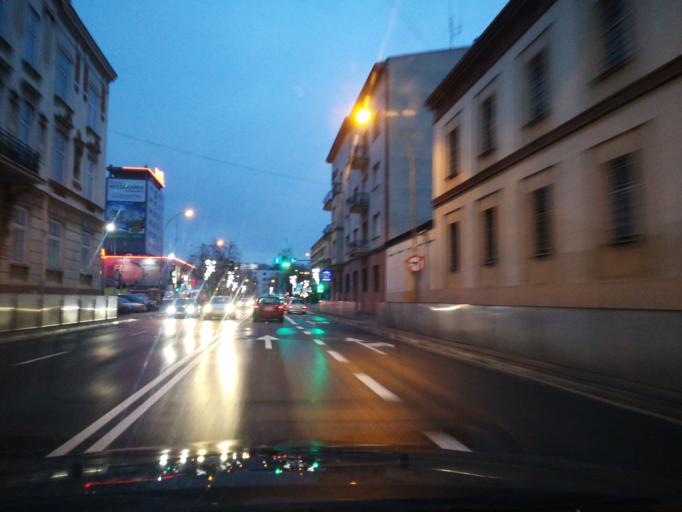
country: PL
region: Subcarpathian Voivodeship
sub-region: Rzeszow
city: Rzeszow
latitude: 50.0346
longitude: 21.9984
